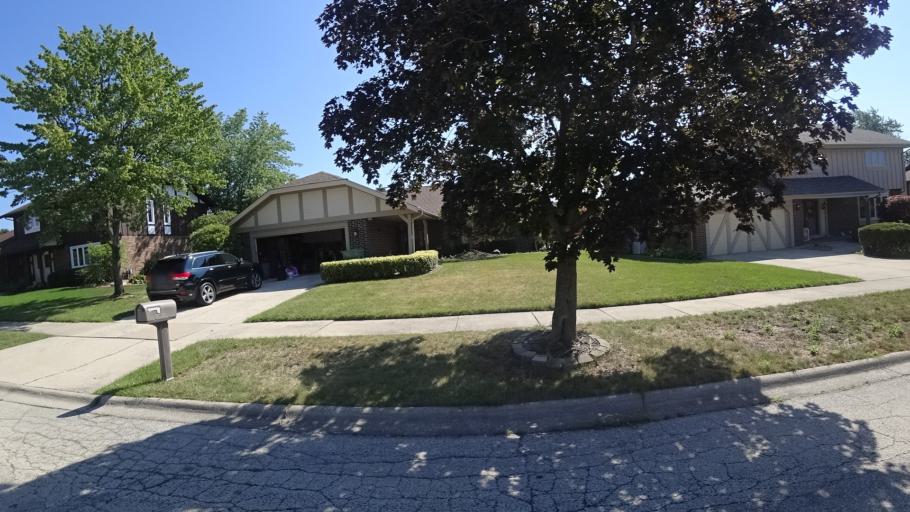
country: US
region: Illinois
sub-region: Cook County
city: Palos Park
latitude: 41.6368
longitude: -87.8180
